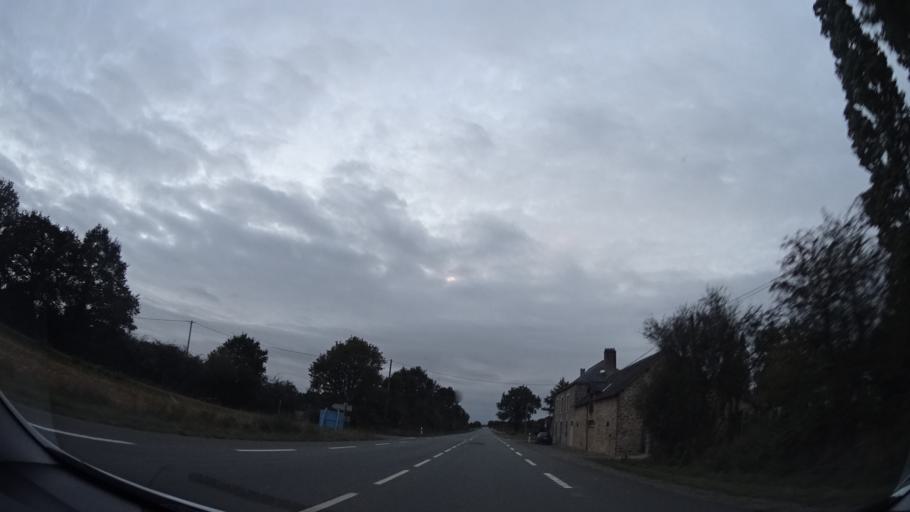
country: FR
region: Pays de la Loire
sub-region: Departement de la Mayenne
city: Vaiges
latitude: 48.0474
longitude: -0.5106
